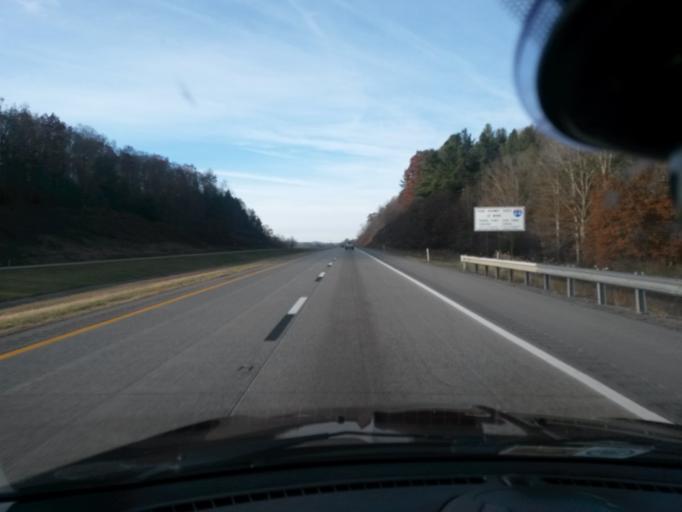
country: US
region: West Virginia
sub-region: Greenbrier County
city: Rainelle
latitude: 37.8802
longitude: -80.6835
